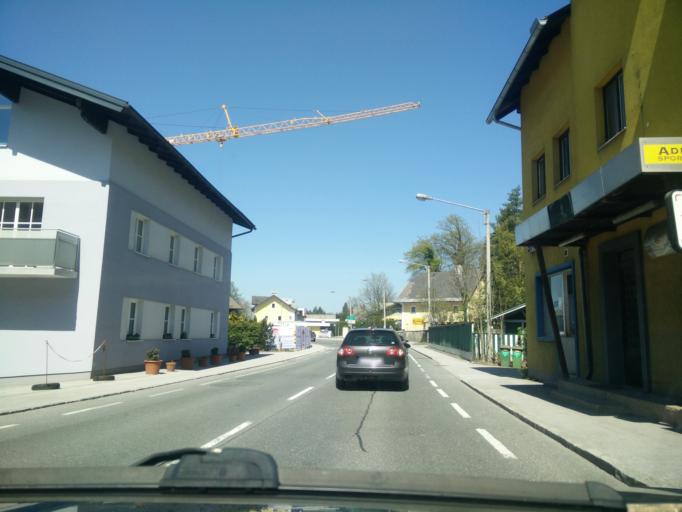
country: AT
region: Salzburg
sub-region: Politischer Bezirk Salzburg-Umgebung
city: Elsbethen
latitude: 47.7693
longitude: 13.0896
